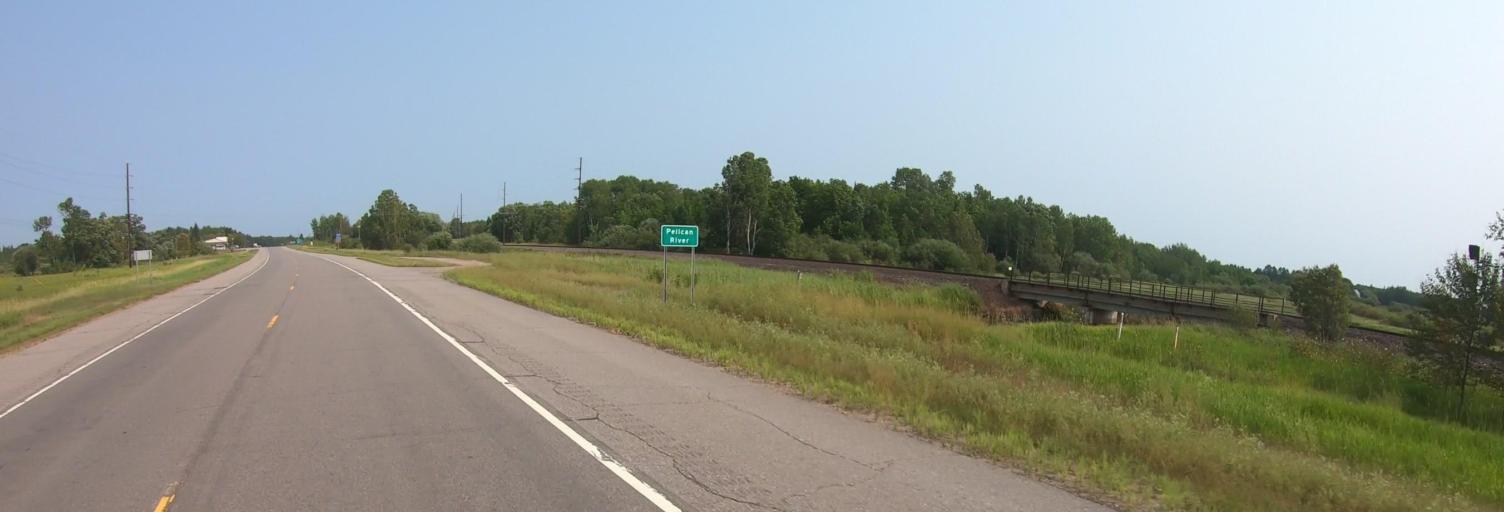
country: US
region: Minnesota
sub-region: Saint Louis County
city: Mountain Iron
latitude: 48.0286
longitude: -92.8301
